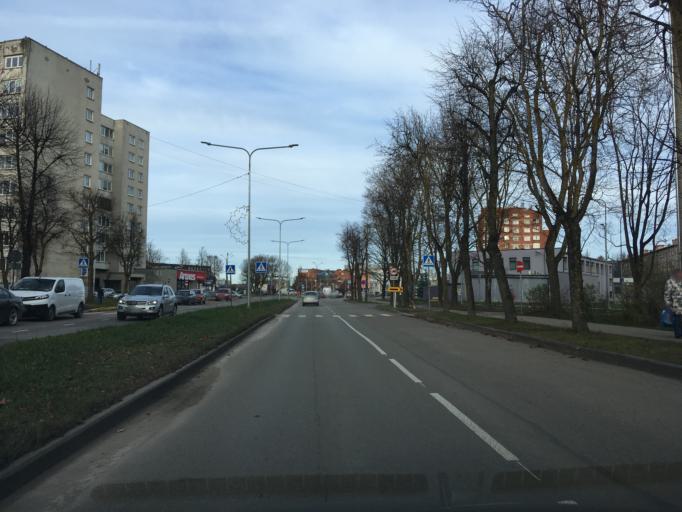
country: EE
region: Ida-Virumaa
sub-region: Narva linn
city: Narva
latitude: 59.3780
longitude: 28.1801
